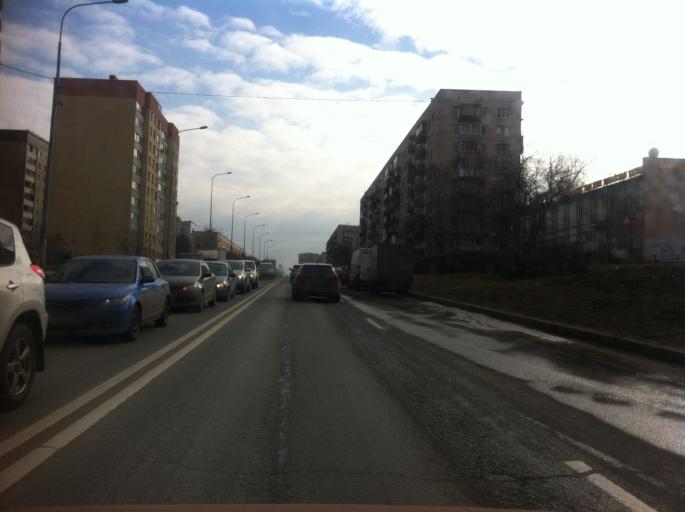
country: RU
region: St.-Petersburg
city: Dachnoye
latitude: 59.8480
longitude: 30.2283
